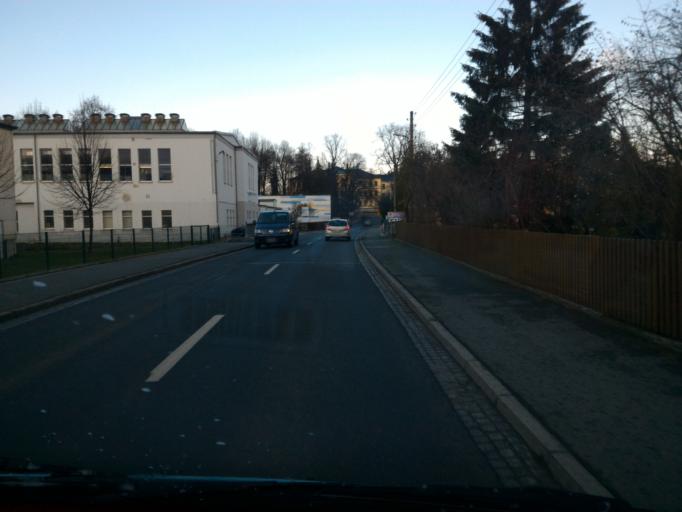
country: DE
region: Saxony
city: Grossschonau
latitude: 50.8944
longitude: 14.6605
